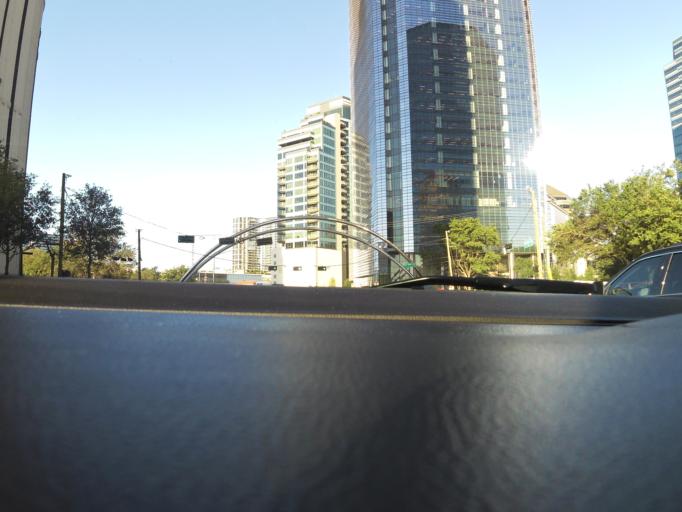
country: US
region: Texas
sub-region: Harris County
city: Hunters Creek Village
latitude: 29.7529
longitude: -95.4596
